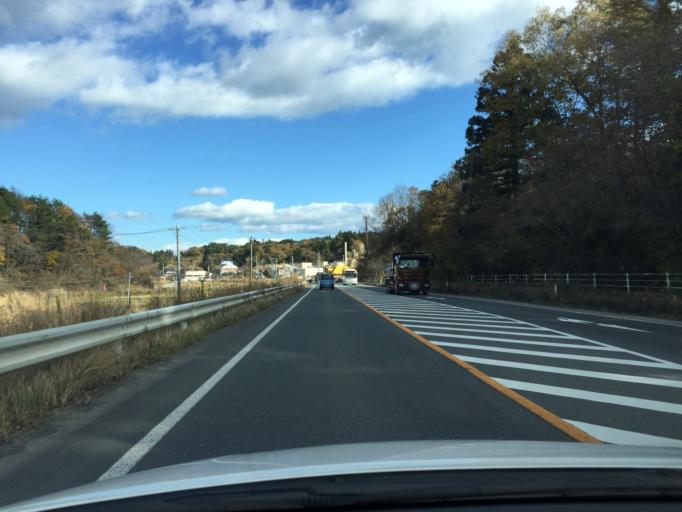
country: JP
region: Fukushima
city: Namie
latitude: 37.5355
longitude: 141.0036
